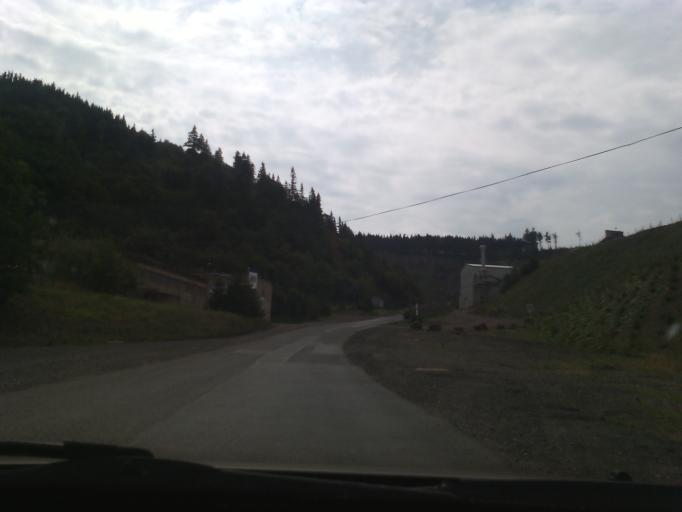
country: CZ
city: Mezimesti
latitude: 50.6946
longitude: 16.2712
